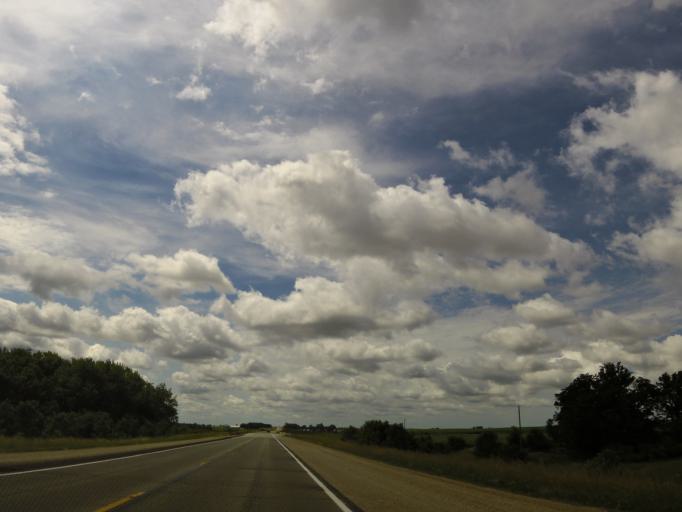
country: US
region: Iowa
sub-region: Chickasaw County
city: New Hampton
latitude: 43.2411
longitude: -92.2990
